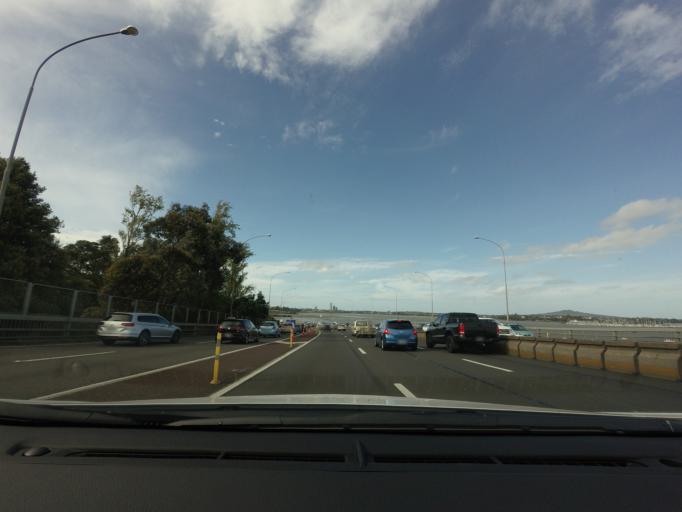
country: NZ
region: Auckland
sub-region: Auckland
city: North Shore
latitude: -36.8244
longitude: 174.7497
